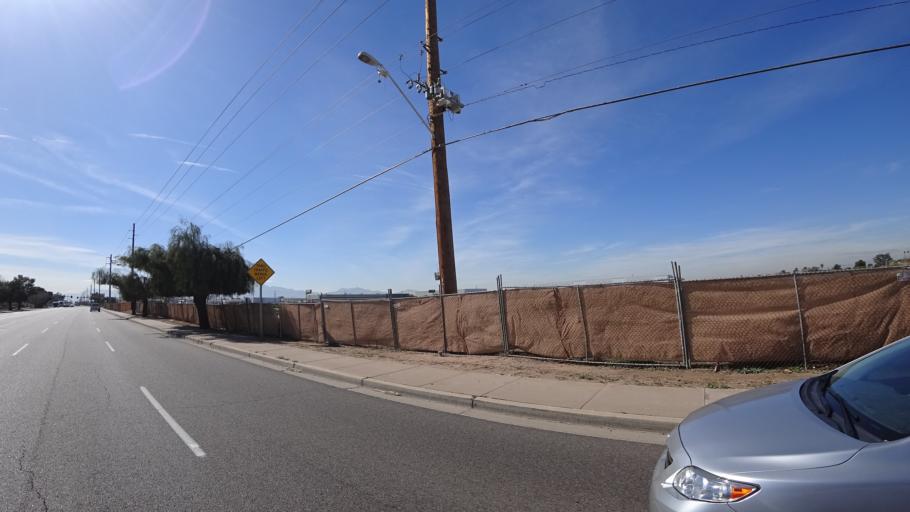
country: US
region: Arizona
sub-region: Maricopa County
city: Tolleson
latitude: 33.4543
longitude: -112.1866
